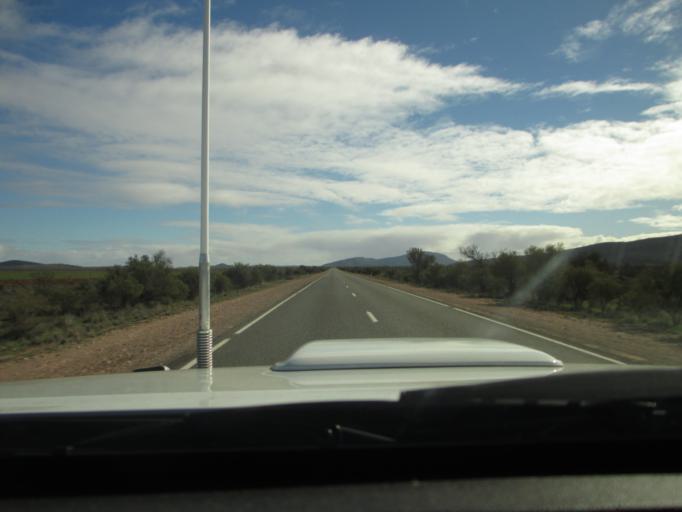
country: AU
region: South Australia
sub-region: Flinders Ranges
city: Quorn
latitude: -31.8601
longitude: 138.4023
